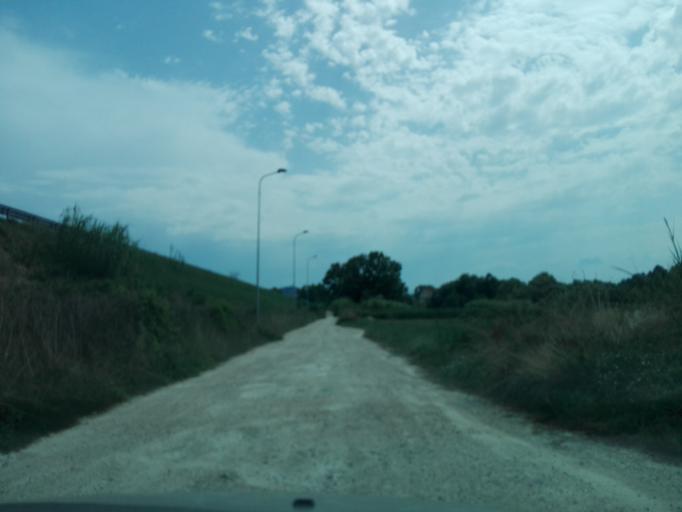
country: IT
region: Abruzzo
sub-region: Provincia di Pescara
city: Cappelle sul Tavo
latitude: 42.4906
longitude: 14.1121
